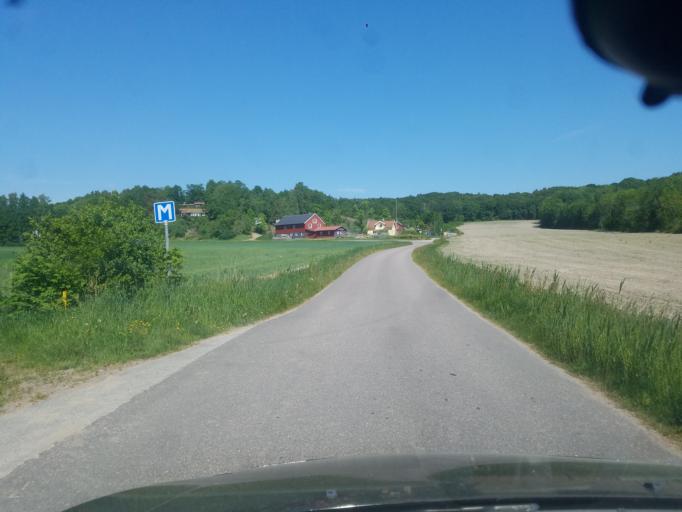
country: SE
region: Vaestra Goetaland
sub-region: Orust
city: Henan
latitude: 58.2661
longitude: 11.5715
